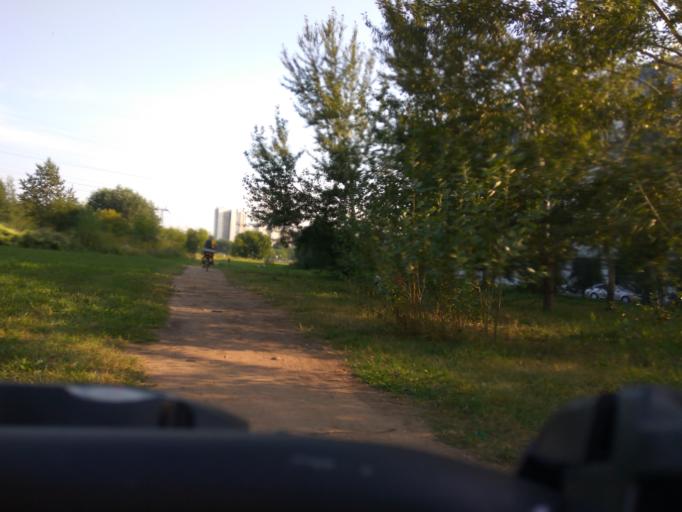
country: RU
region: Moscow
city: Brateyevo
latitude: 55.6508
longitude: 37.7720
